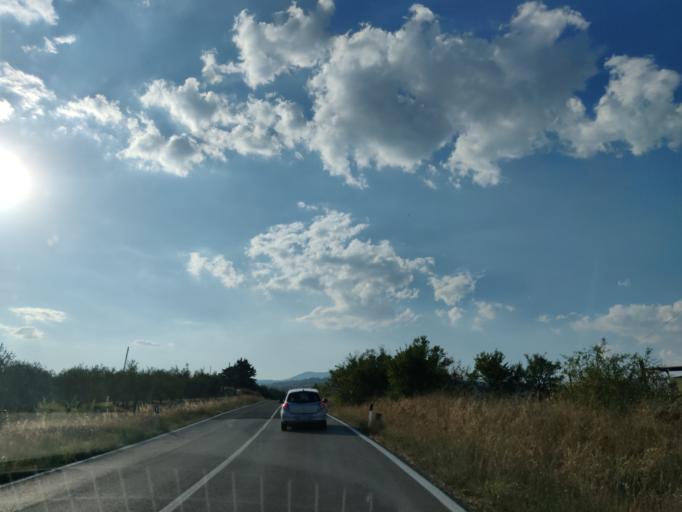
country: IT
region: Tuscany
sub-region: Provincia di Siena
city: Piancastagnaio
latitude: 42.8326
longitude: 11.7186
